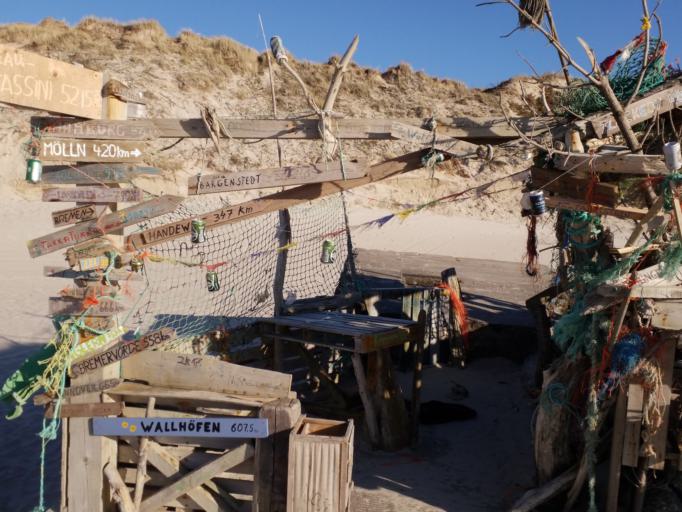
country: DK
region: North Denmark
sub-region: Jammerbugt Kommune
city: Pandrup
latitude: 57.3799
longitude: 9.7174
